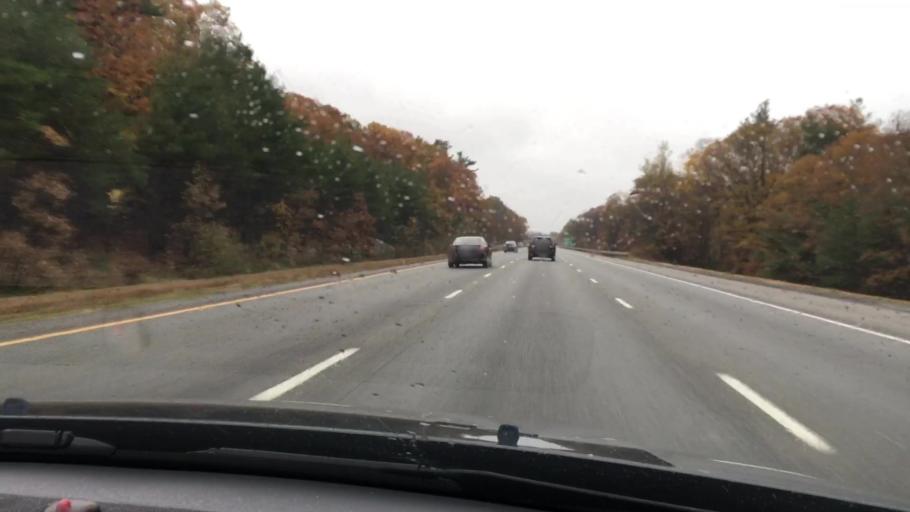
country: US
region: Massachusetts
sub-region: Worcester County
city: Bolton
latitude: 42.4233
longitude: -71.5997
